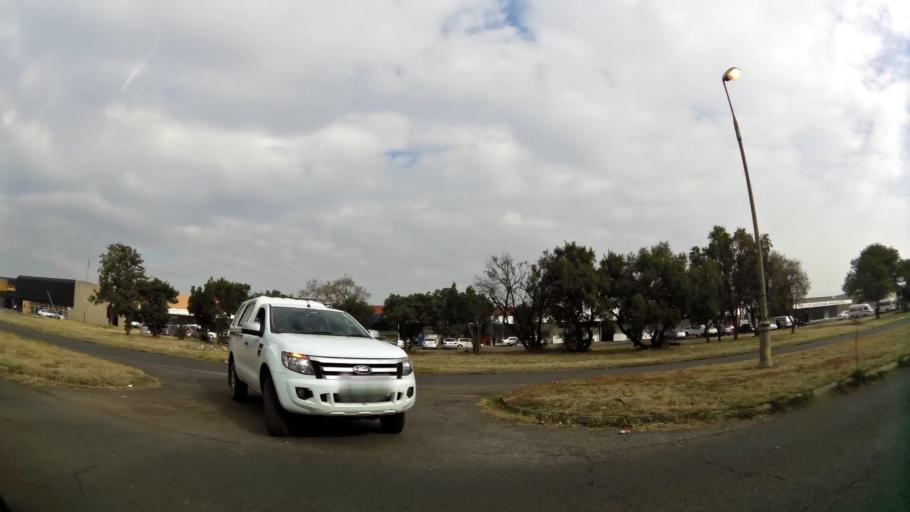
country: ZA
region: Gauteng
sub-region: Sedibeng District Municipality
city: Vanderbijlpark
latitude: -26.6963
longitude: 27.8404
